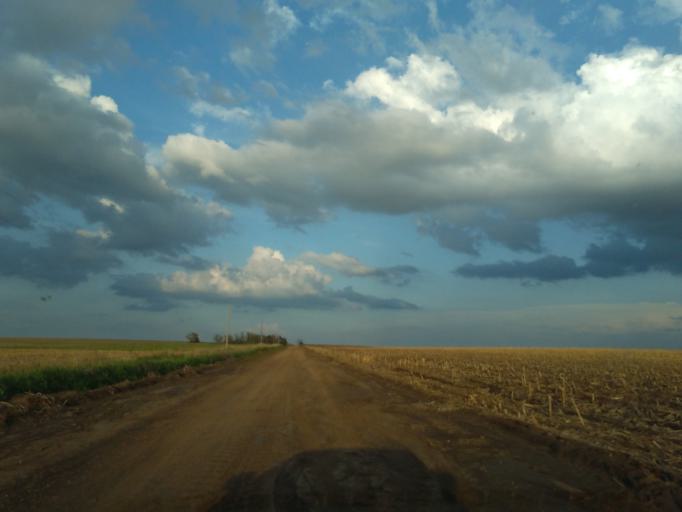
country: US
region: Nebraska
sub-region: Webster County
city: Red Cloud
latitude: 40.2053
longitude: -98.4022
